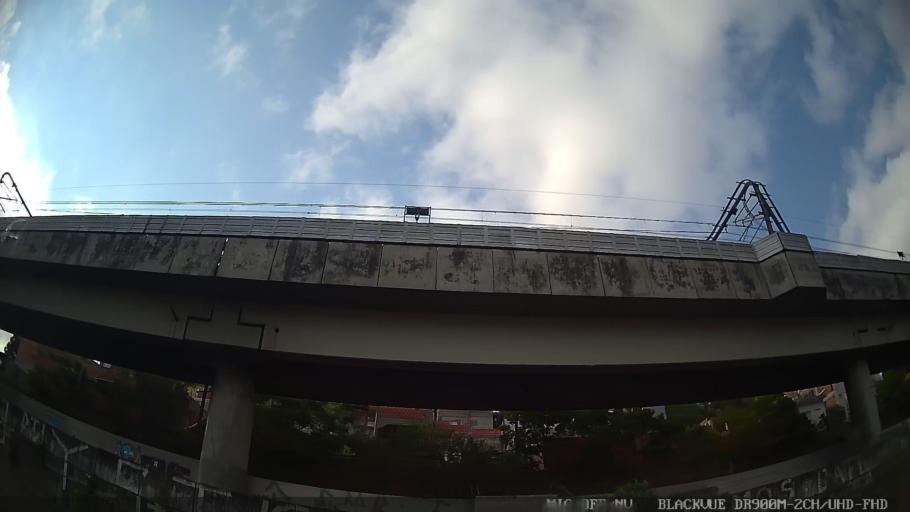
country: BR
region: Sao Paulo
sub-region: Taboao Da Serra
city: Taboao da Serra
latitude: -23.6393
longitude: -46.7433
